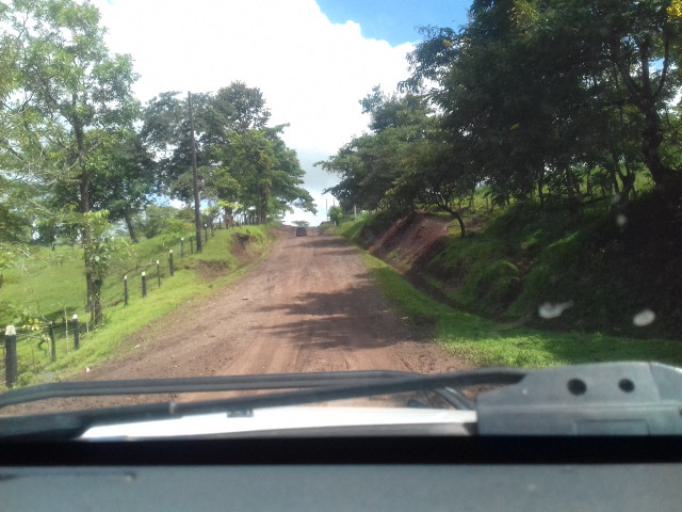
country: NI
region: Matagalpa
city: Rio Blanco
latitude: 12.9783
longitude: -85.1847
